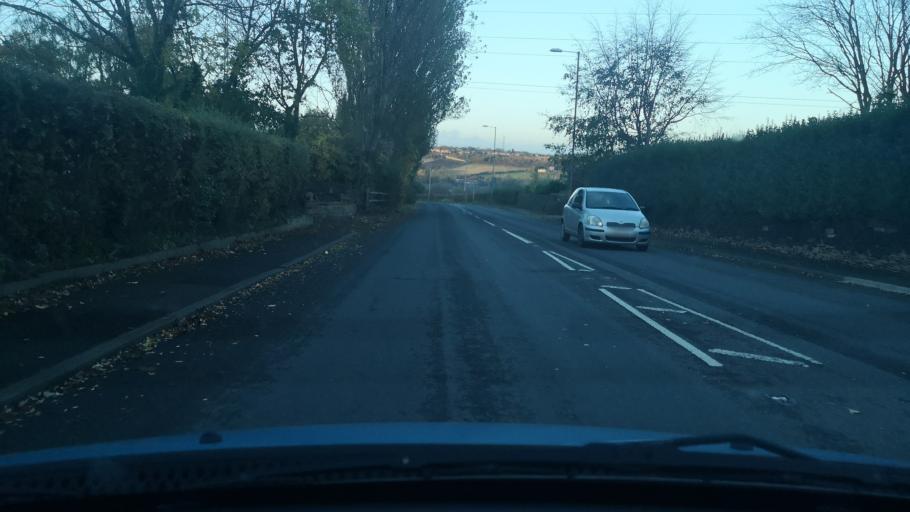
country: GB
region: England
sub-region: City and Borough of Wakefield
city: Horbury
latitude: 53.6505
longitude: -1.5740
